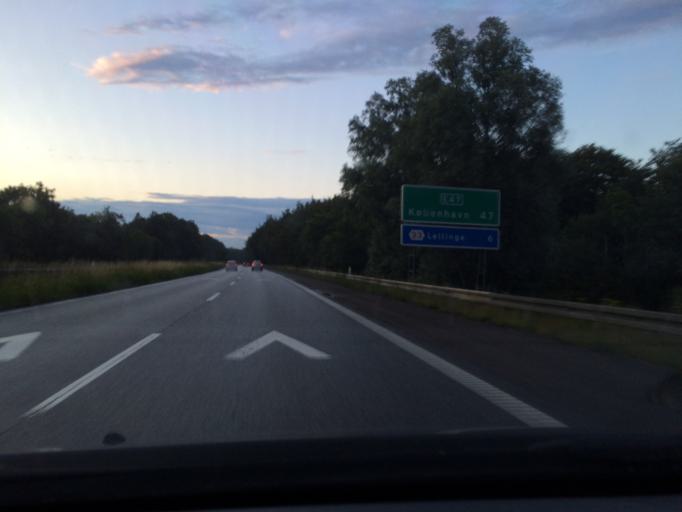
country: DK
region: Zealand
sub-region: Koge Kommune
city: Ejby
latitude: 55.4089
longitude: 12.1008
